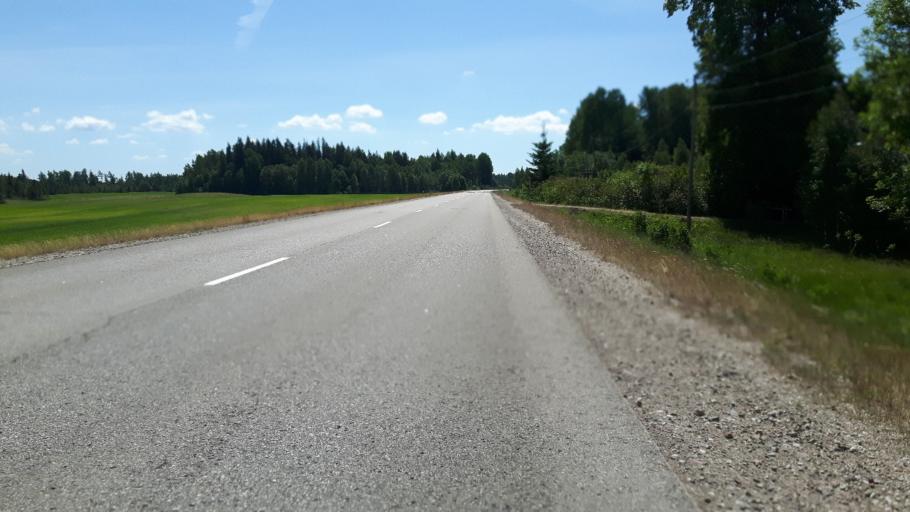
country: LV
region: Kuldigas Rajons
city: Kuldiga
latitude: 56.9133
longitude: 21.9051
